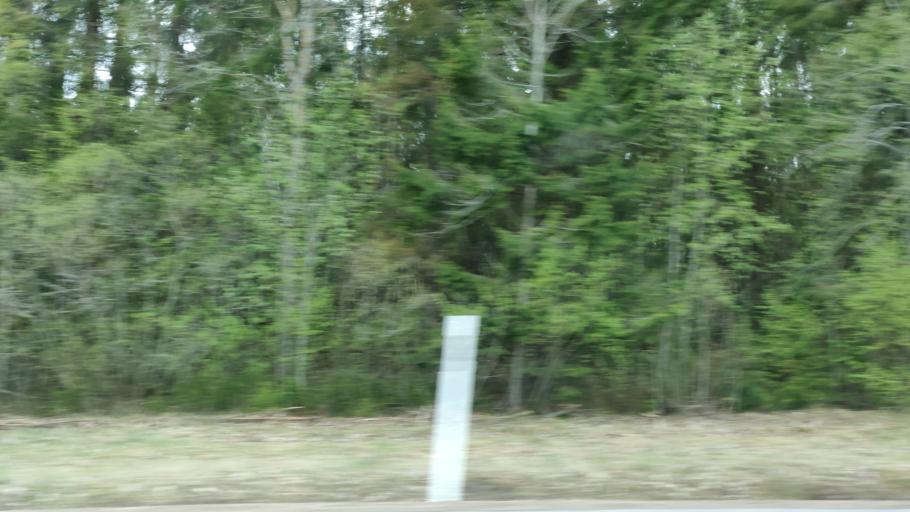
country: SE
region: Vaermland
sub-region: Forshaga Kommun
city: Deje
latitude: 59.6251
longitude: 13.4430
